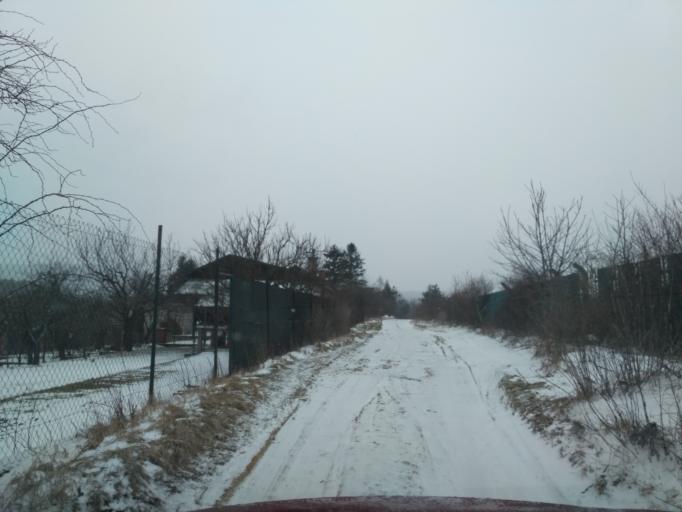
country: SK
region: Kosicky
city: Kosice
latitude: 48.7197
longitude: 21.2213
